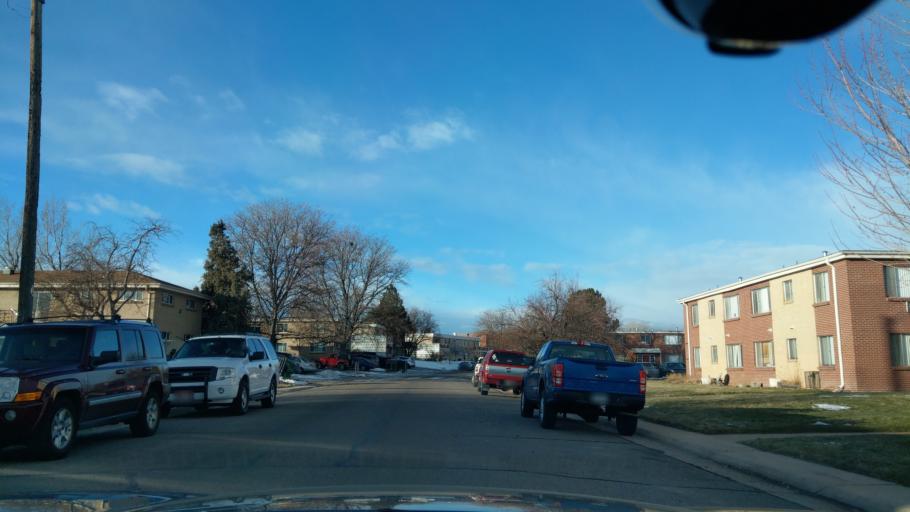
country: US
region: Colorado
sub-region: Jefferson County
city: Lakewood
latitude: 39.7298
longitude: -105.1160
